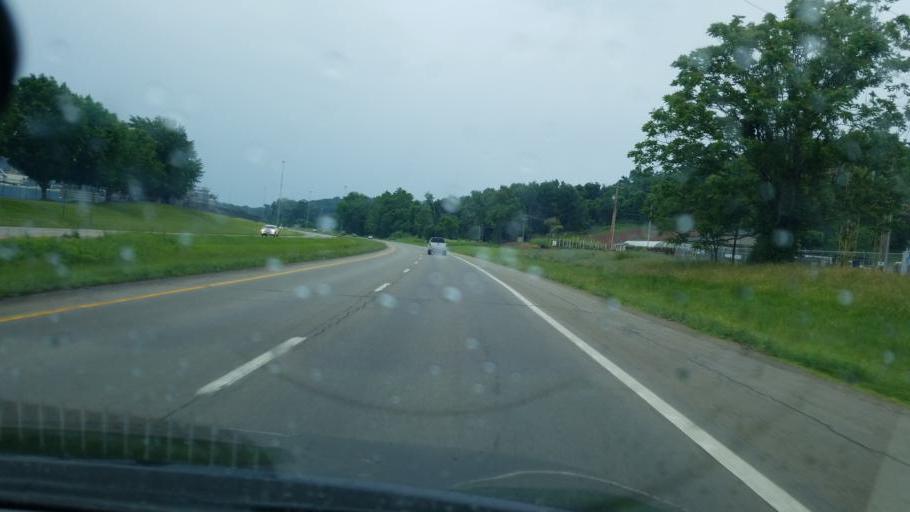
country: US
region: West Virginia
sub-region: Wood County
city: Blennerhassett
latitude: 39.2840
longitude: -81.6331
